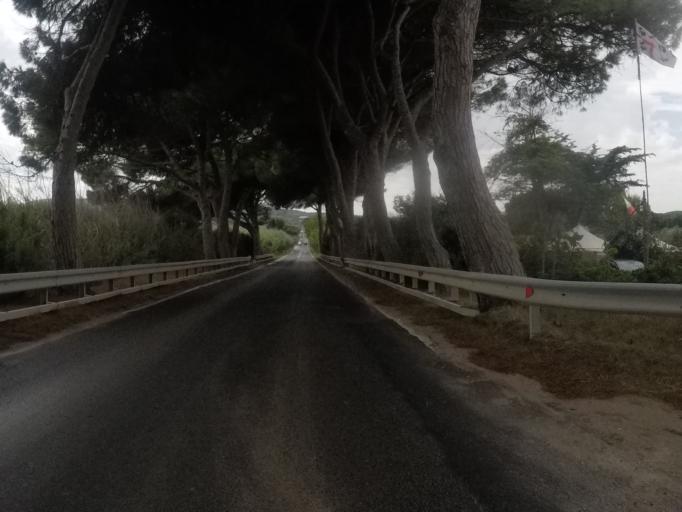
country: IT
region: Sardinia
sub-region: Provincia di Sassari
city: Sorso
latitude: 40.8331
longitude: 8.5951
